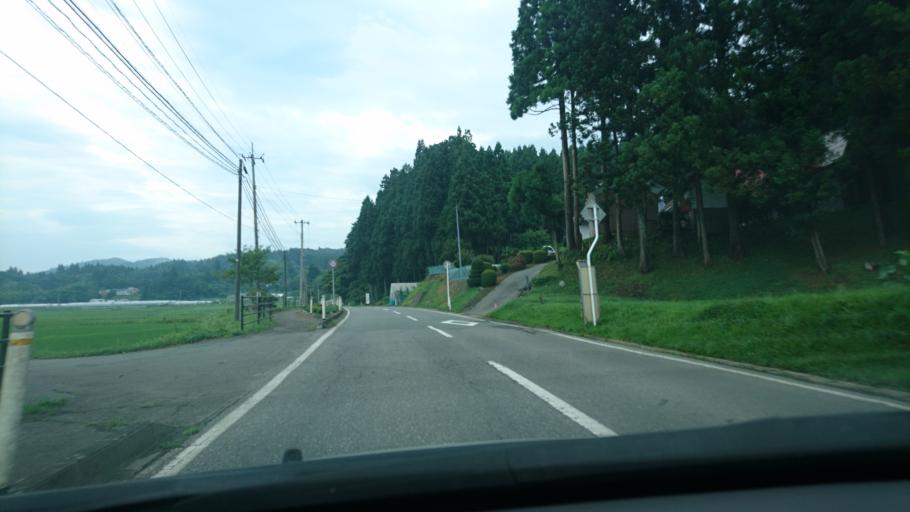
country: JP
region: Iwate
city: Ichinoseki
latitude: 38.9312
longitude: 141.4235
